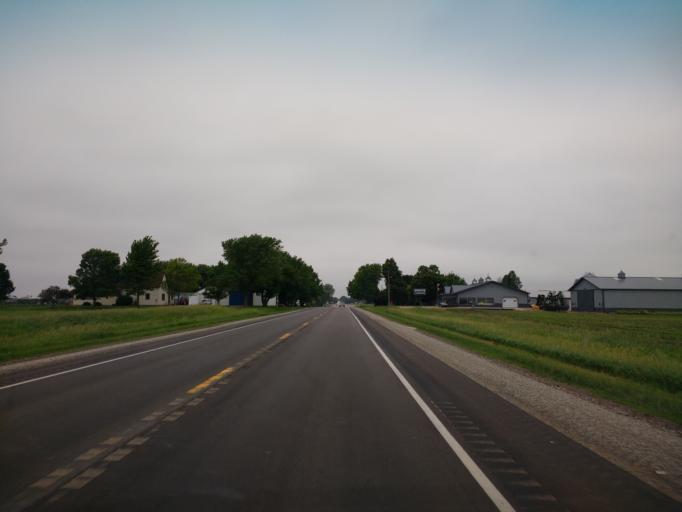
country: US
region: Iowa
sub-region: O'Brien County
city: Sanborn
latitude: 43.1861
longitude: -95.6361
